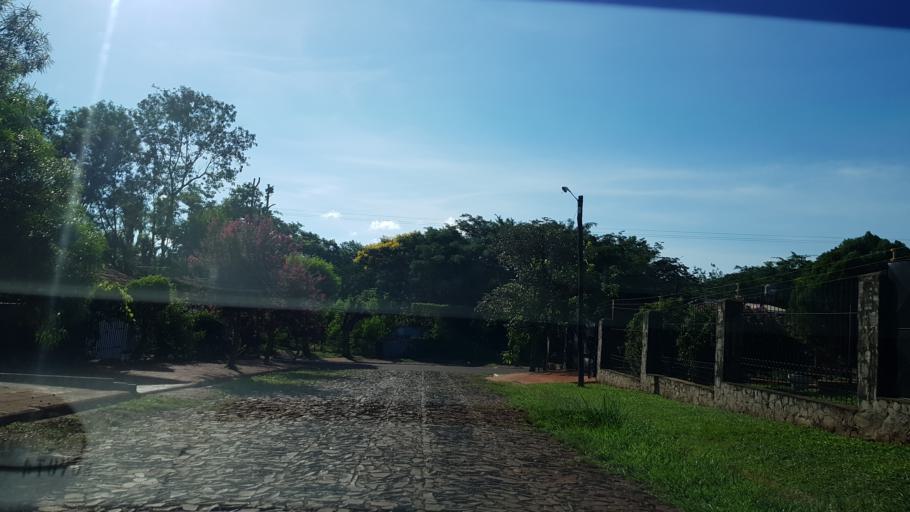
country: AR
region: Misiones
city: Puerto Libertad
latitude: -25.9203
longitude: -54.5785
